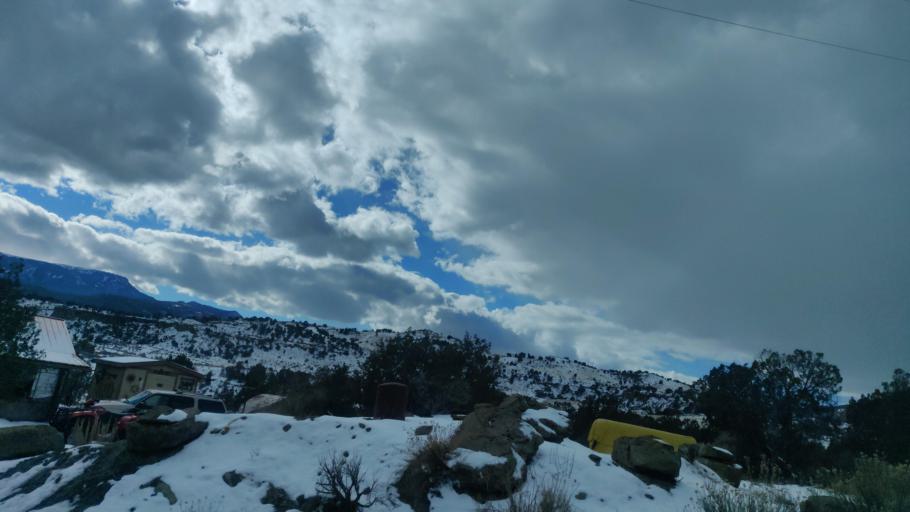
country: US
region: Colorado
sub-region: Mesa County
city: Palisade
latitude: 39.2078
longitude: -108.1477
